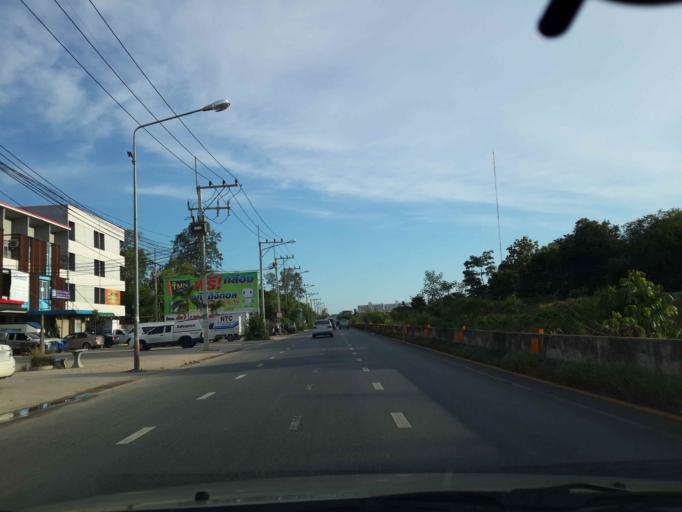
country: TH
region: Chon Buri
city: Phatthaya
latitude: 12.9427
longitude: 100.9110
